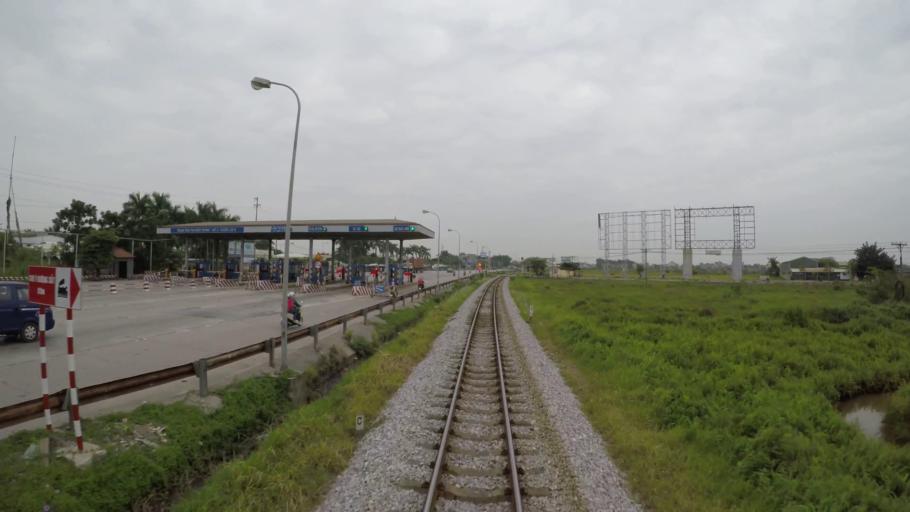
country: VN
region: Hai Duong
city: Phu Thai
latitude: 20.9264
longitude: 106.5566
